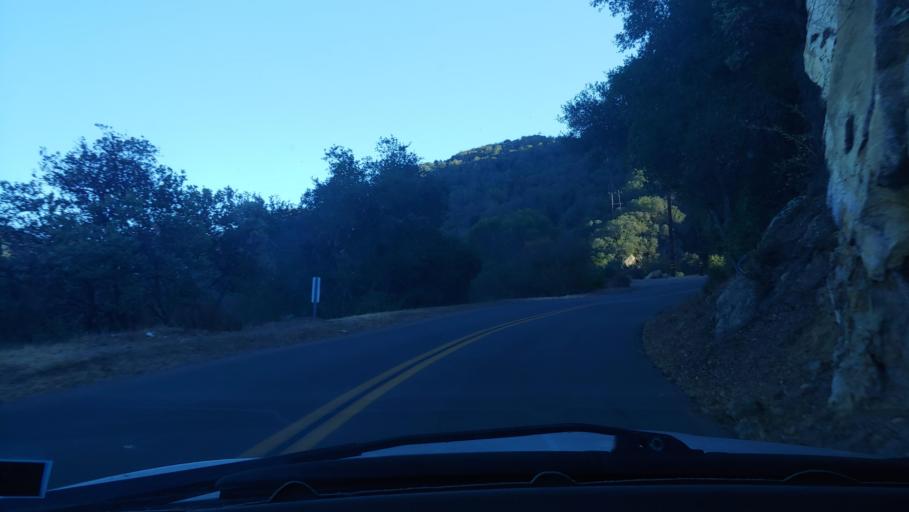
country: US
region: California
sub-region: Santa Barbara County
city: Goleta
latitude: 34.5286
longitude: -119.8333
